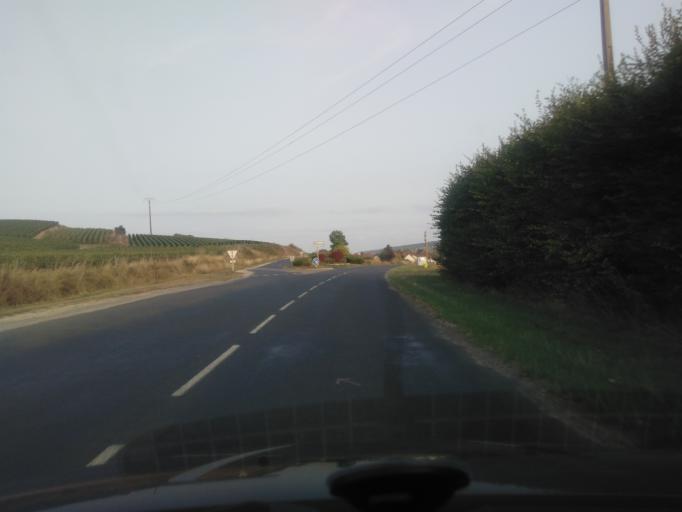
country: FR
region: Champagne-Ardenne
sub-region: Departement de la Marne
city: Mareuil-le-Port
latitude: 49.0859
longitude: 3.7925
